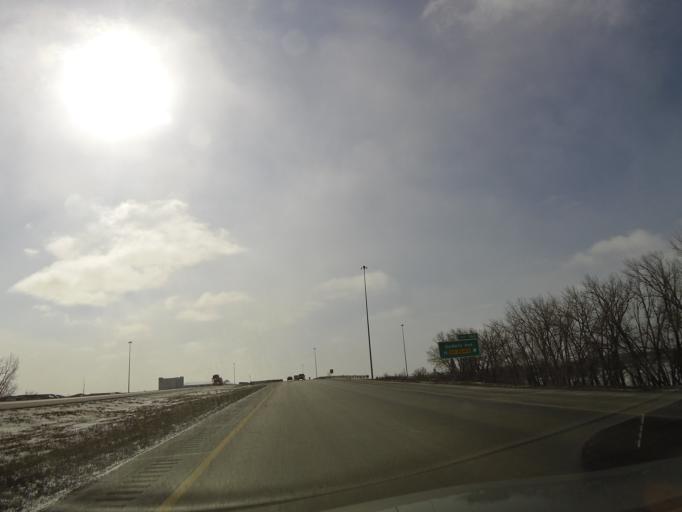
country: US
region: North Dakota
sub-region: Grand Forks County
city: Grand Forks
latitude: 47.9207
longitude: -97.0937
